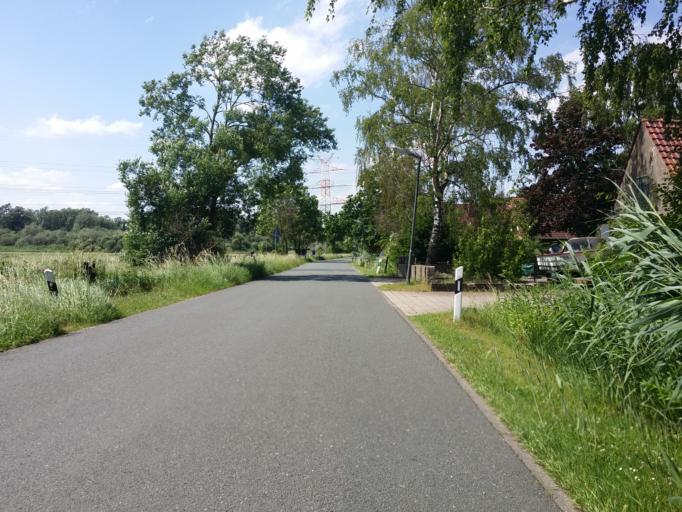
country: DE
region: Lower Saxony
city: Lemwerder
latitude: 53.1192
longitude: 8.6754
